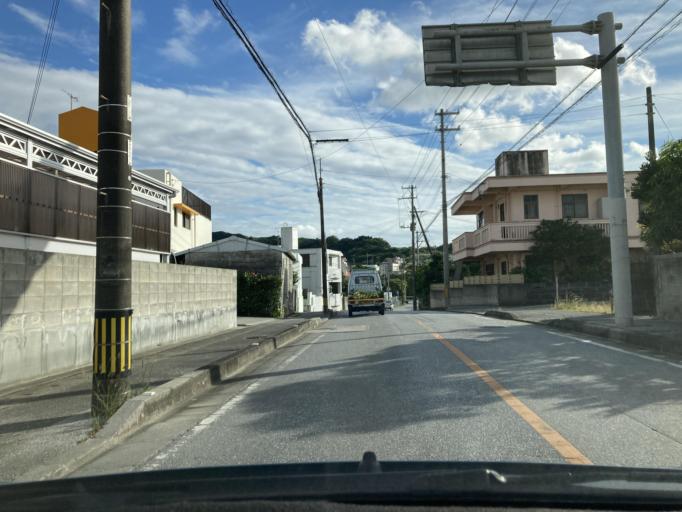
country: JP
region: Okinawa
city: Itoman
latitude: 26.1363
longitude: 127.6986
